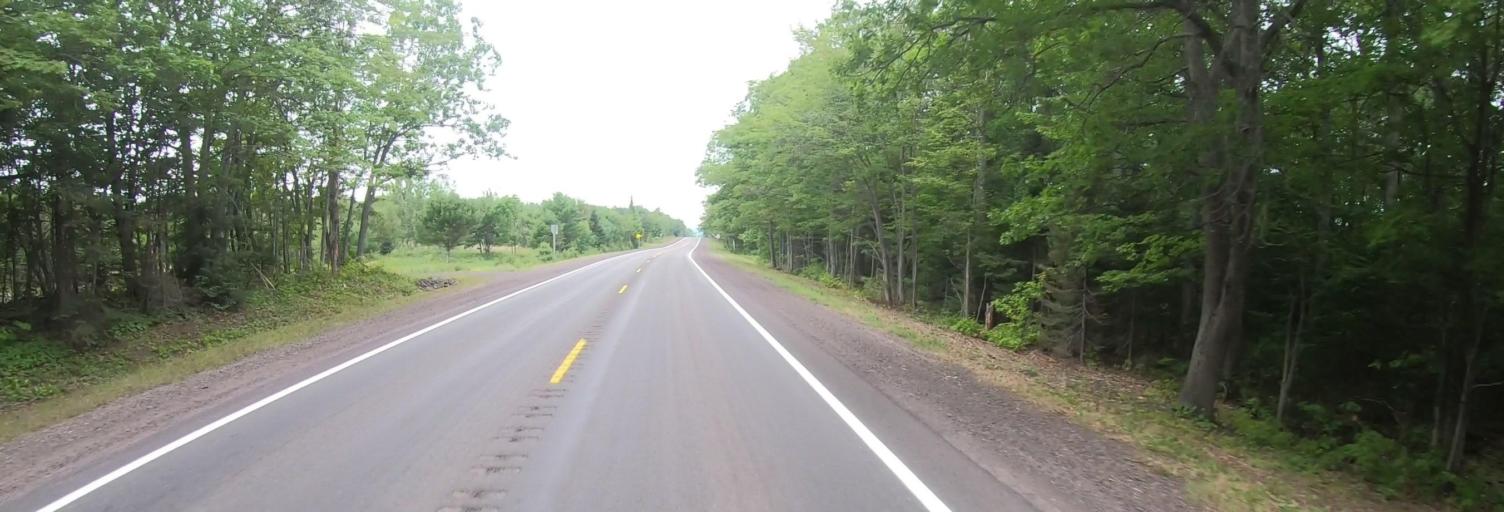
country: US
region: Michigan
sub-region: Keweenaw County
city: Eagle River
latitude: 47.3193
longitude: -88.3416
